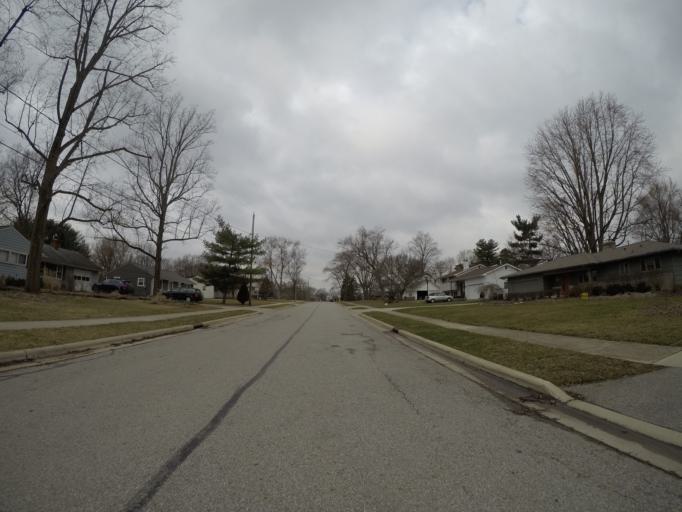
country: US
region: Ohio
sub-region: Franklin County
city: Upper Arlington
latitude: 40.0228
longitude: -83.0823
